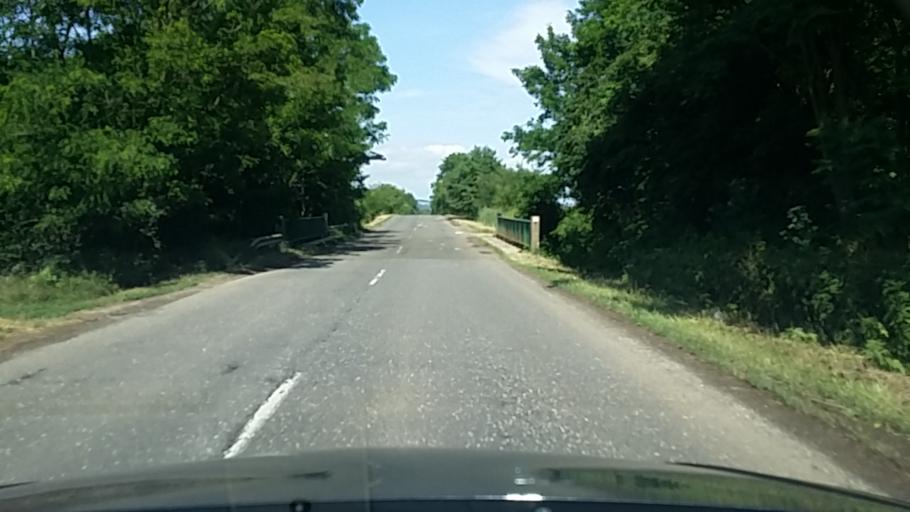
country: SK
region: Nitriansky
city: Sahy
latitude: 48.0577
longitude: 18.9355
